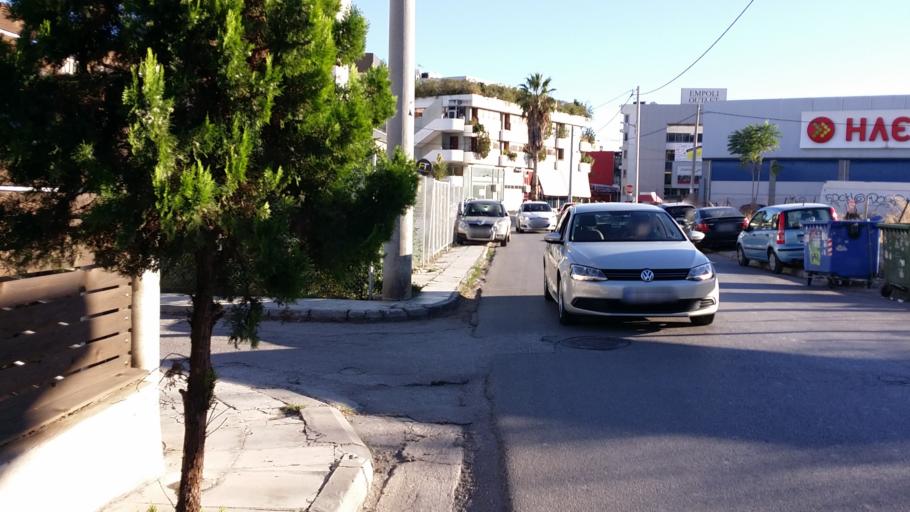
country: GR
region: Attica
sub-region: Nomarchia Athinas
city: Irakleio
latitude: 38.0514
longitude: 23.7520
